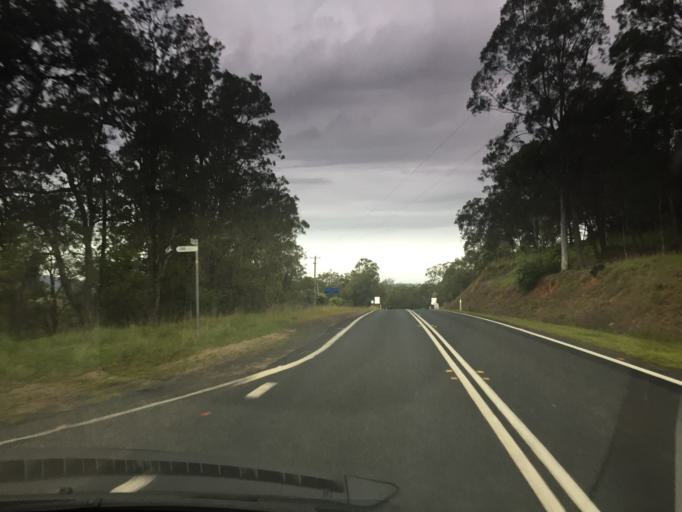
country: AU
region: New South Wales
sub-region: Bega Valley
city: Bega
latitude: -36.6313
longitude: 149.5748
